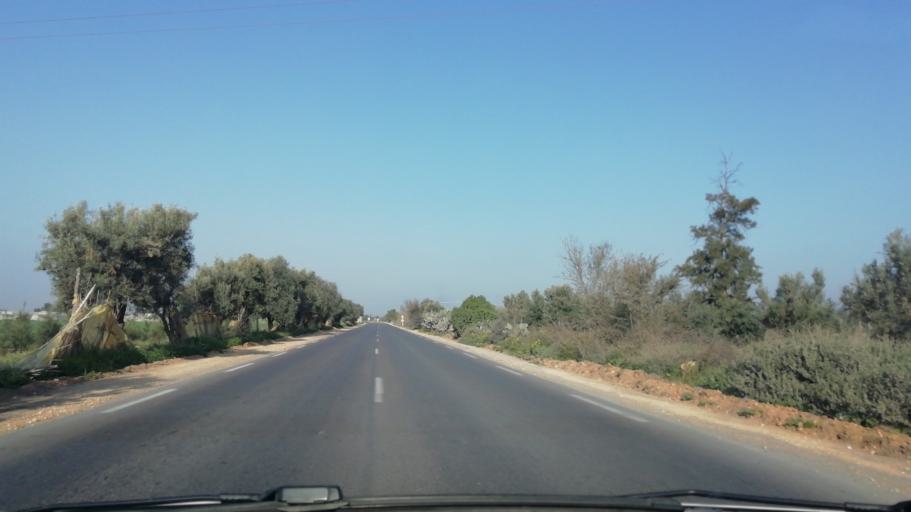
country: DZ
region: Mostaganem
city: Mostaganem
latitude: 35.7551
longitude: 0.1127
